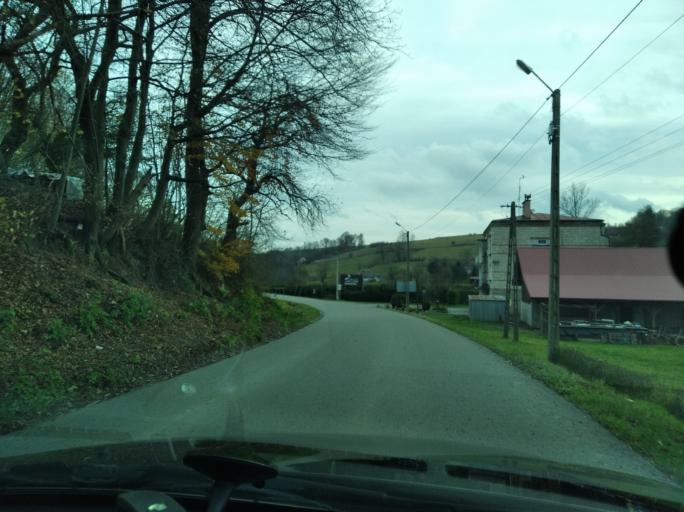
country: PL
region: Subcarpathian Voivodeship
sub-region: Powiat ropczycko-sedziszowski
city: Iwierzyce
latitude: 49.9485
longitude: 21.7304
